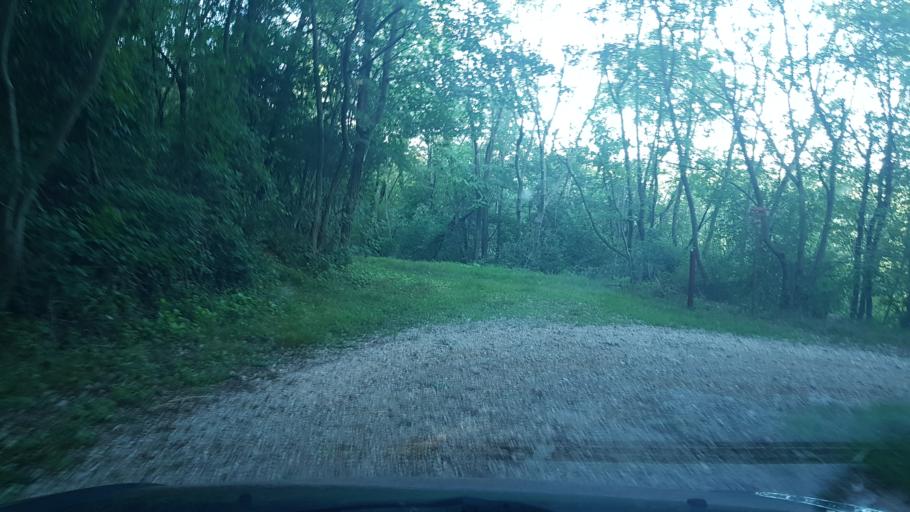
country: SI
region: Kanal
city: Deskle
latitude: 46.0230
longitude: 13.6220
